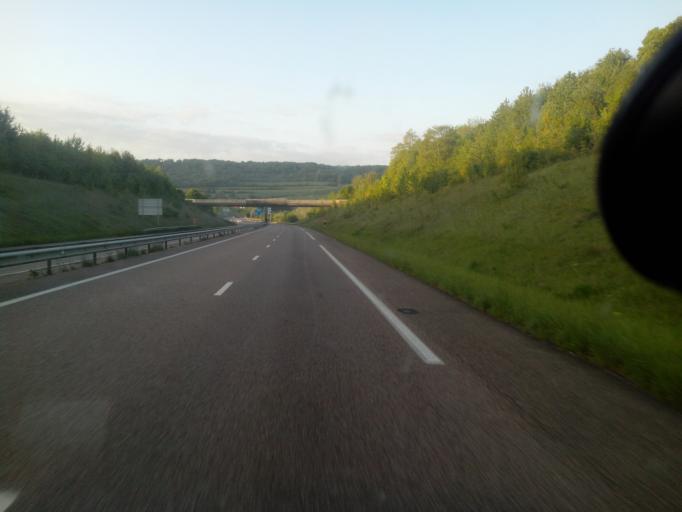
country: FR
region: Picardie
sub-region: Departement de la Somme
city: Bouttencourt
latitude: 49.9225
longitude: 1.6377
